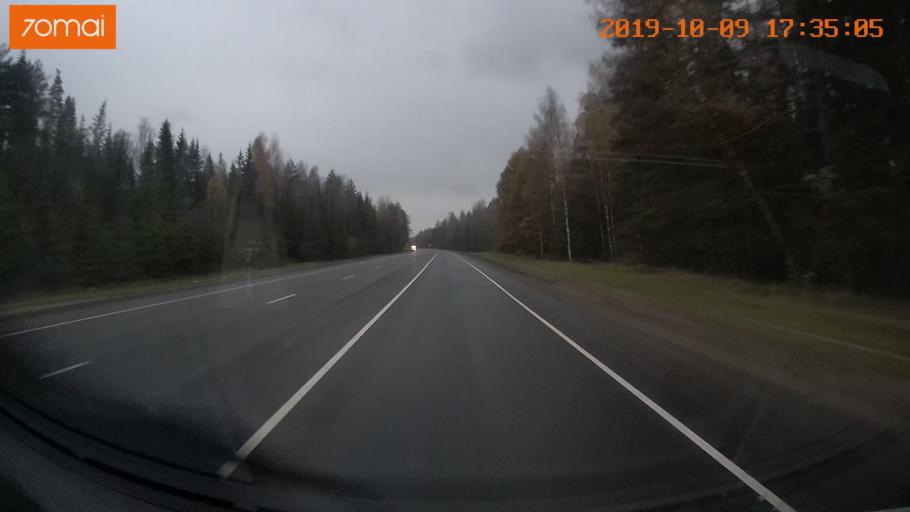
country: RU
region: Ivanovo
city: Bogorodskoye
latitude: 57.0990
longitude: 41.0051
